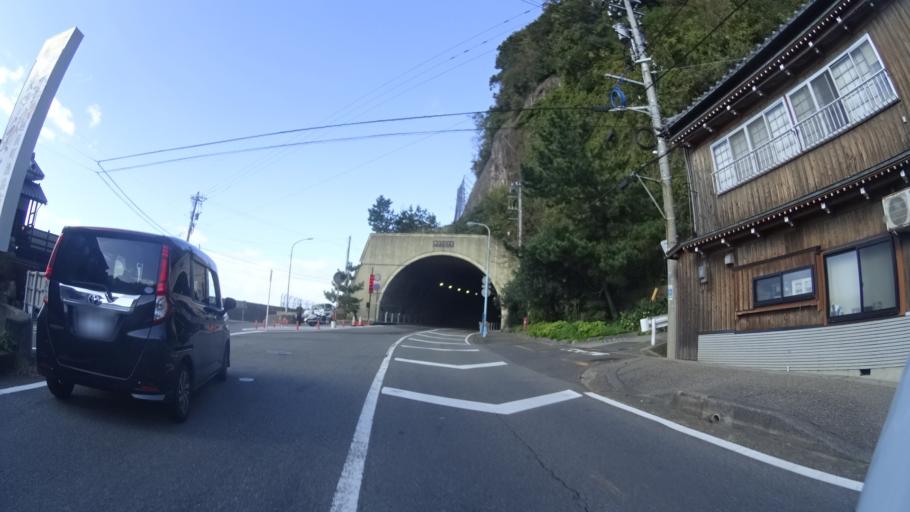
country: JP
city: Asahi
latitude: 35.9429
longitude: 135.9891
